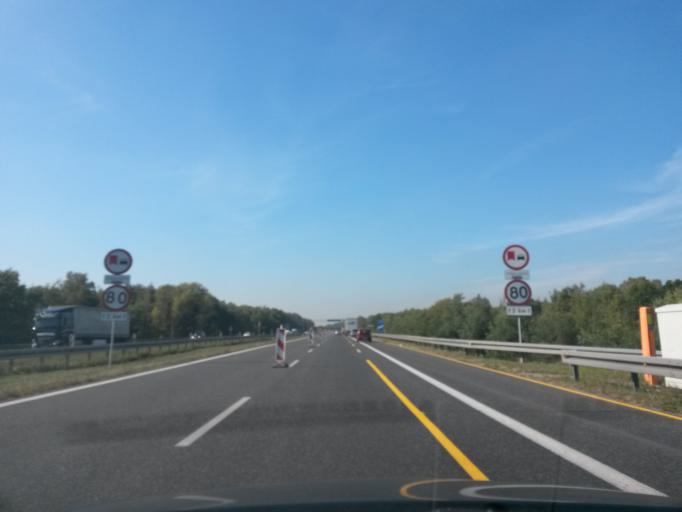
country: PL
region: Silesian Voivodeship
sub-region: Myslowice
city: Myslowice
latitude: 50.2132
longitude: 19.1431
